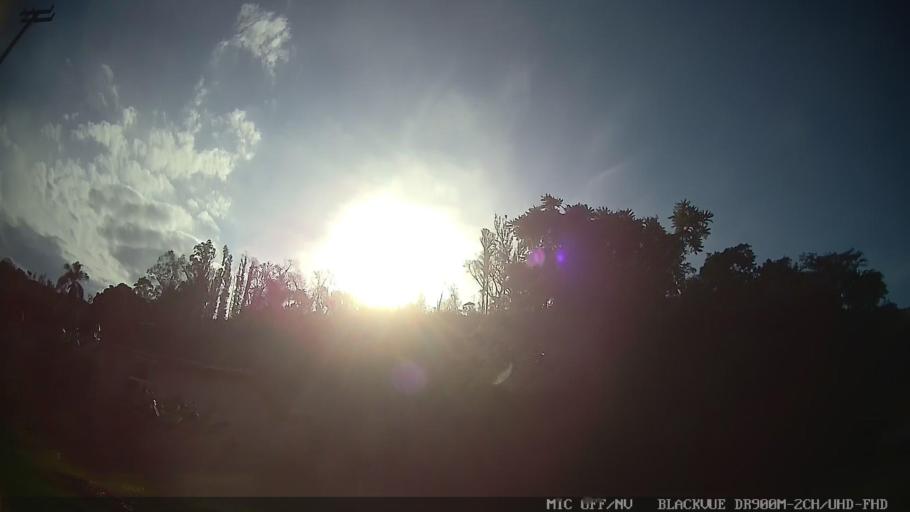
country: BR
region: Sao Paulo
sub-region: Serra Negra
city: Serra Negra
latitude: -22.6783
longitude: -46.6807
